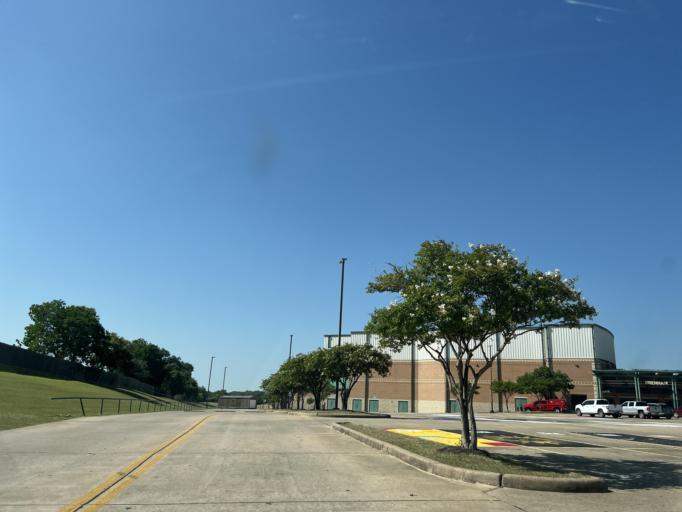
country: US
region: Texas
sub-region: Washington County
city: Brenham
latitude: 30.1811
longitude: -96.3973
